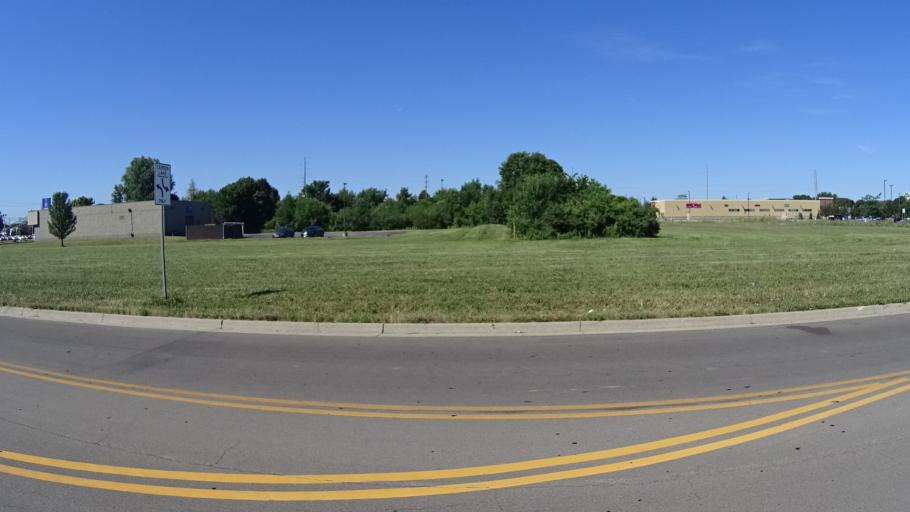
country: US
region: Ohio
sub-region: Erie County
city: Sandusky
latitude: 41.4237
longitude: -82.6757
